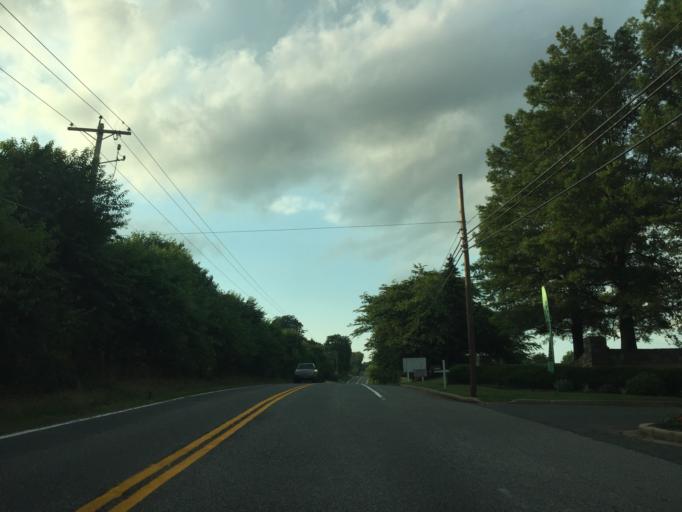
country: US
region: Maryland
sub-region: Harford County
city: Jarrettsville
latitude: 39.5708
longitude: -76.4996
